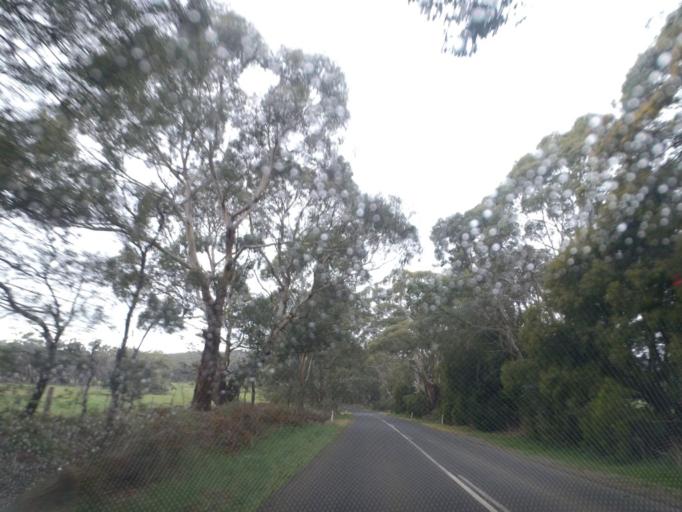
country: AU
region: Victoria
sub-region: Hume
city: Sunbury
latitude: -37.3521
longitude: 144.6474
